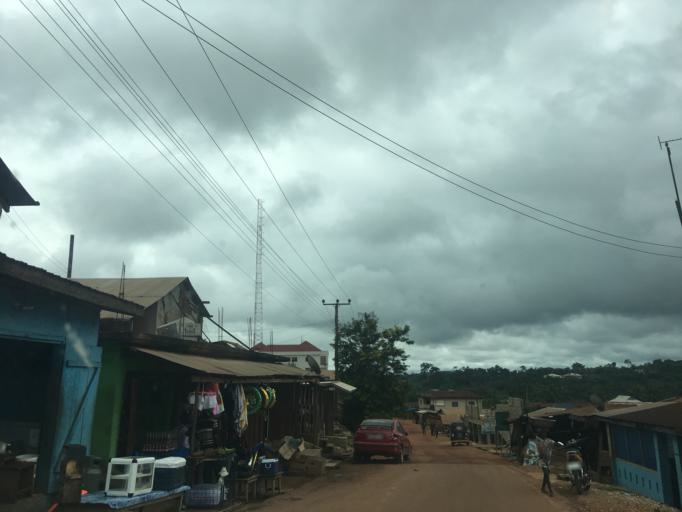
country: GH
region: Western
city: Wassa-Akropong
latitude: 5.8103
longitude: -2.4354
